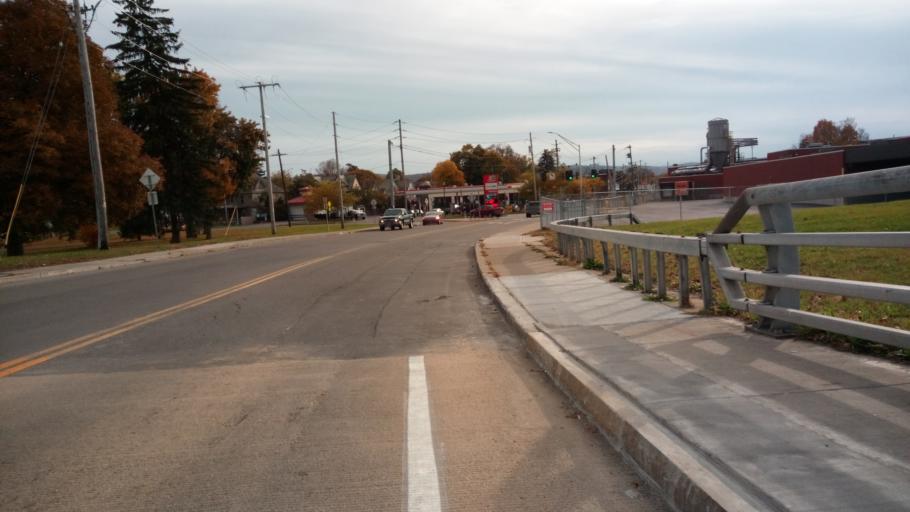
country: US
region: New York
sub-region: Chemung County
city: Elmira
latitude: 42.0867
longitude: -76.7982
